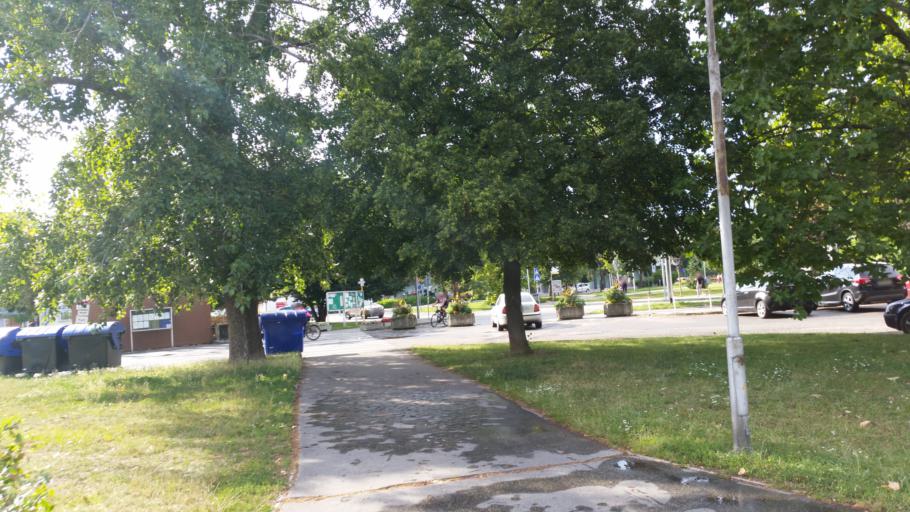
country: SK
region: Trnavsky
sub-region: Okres Trnava
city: Piestany
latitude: 48.5866
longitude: 17.8343
